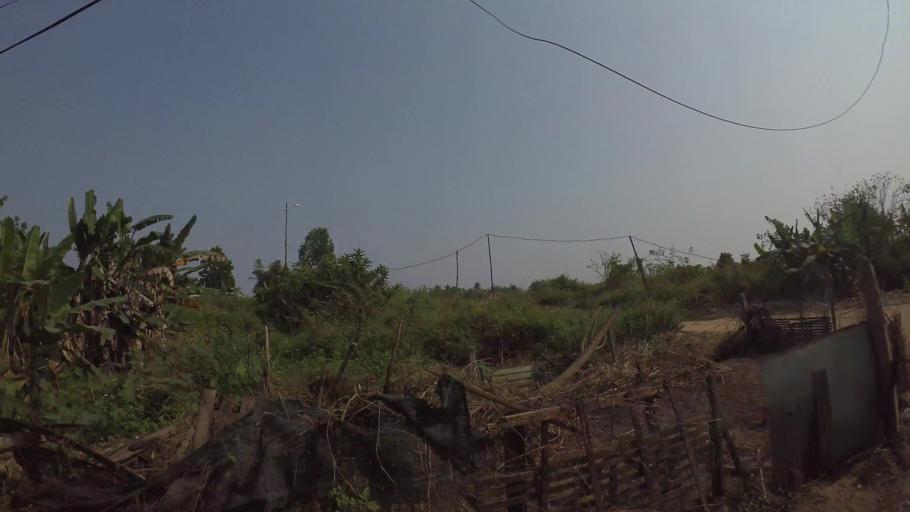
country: VN
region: Da Nang
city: Cam Le
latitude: 16.0012
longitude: 108.1923
